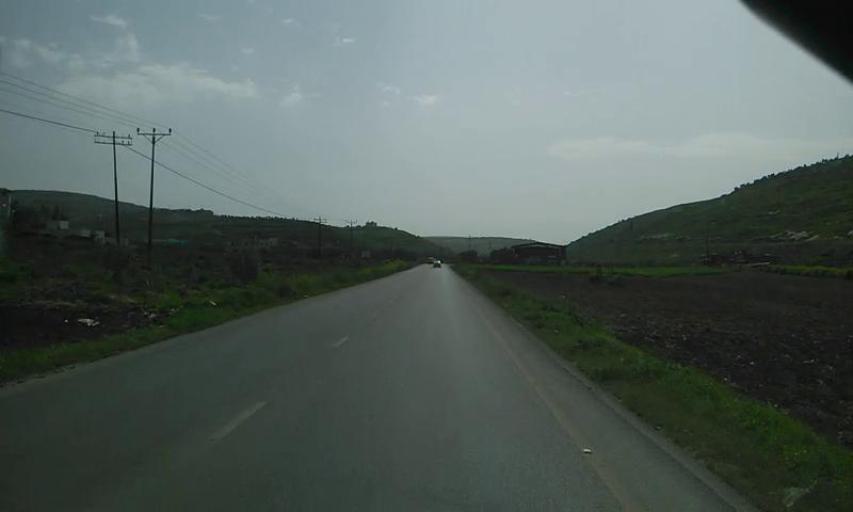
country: PS
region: West Bank
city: Mirkah
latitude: 32.3952
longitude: 35.2212
